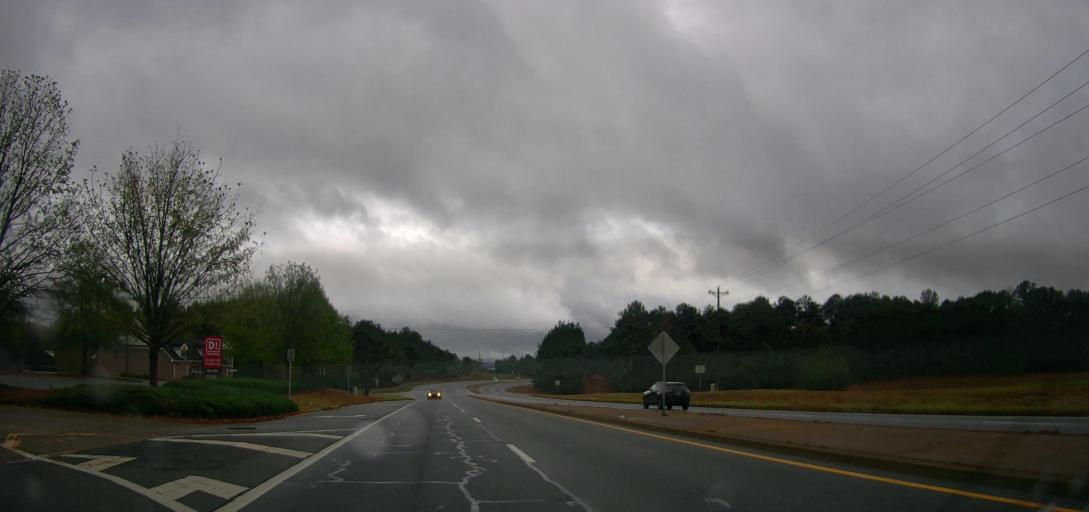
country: US
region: Georgia
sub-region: Oconee County
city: Watkinsville
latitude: 33.8869
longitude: -83.4137
